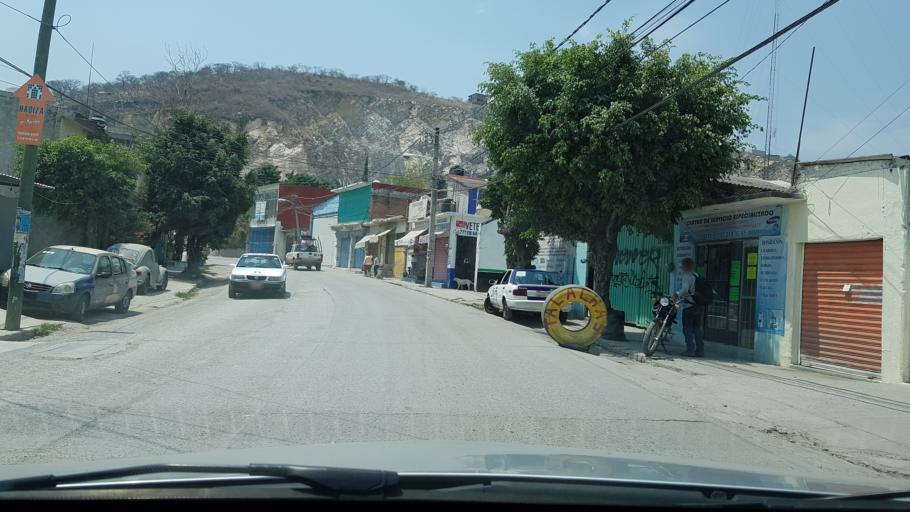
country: MX
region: Morelos
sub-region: Jiutepec
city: Calera Chica
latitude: 18.8579
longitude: -99.1800
